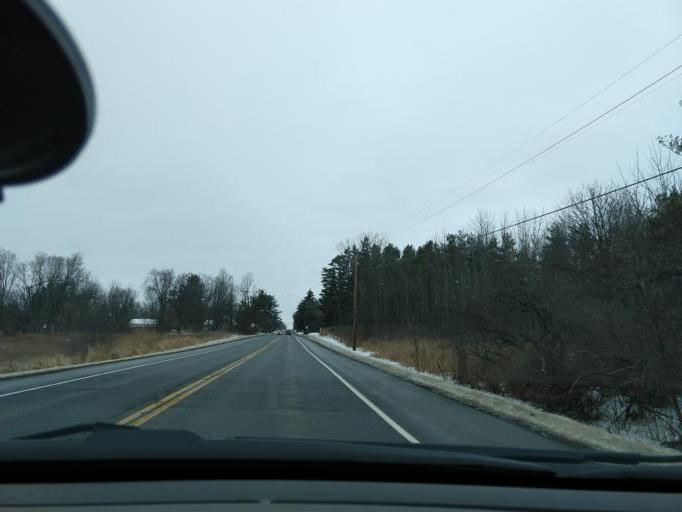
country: US
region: New York
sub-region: Tompkins County
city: Lansing
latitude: 42.5242
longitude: -76.4917
